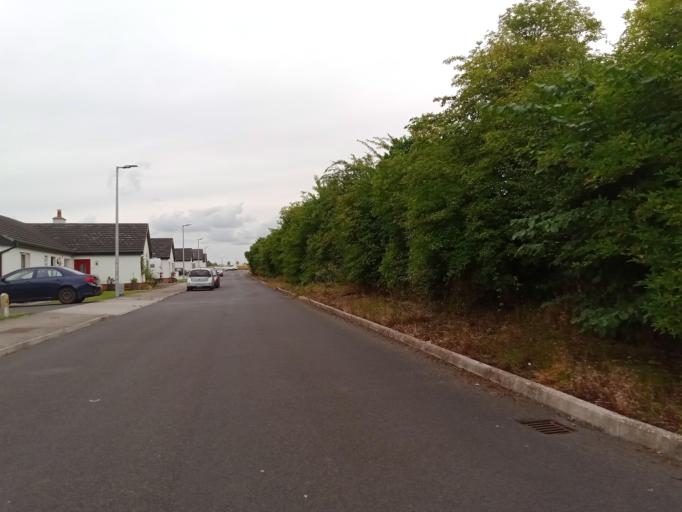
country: IE
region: Leinster
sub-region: Kilkenny
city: Callan
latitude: 52.5483
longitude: -7.3830
